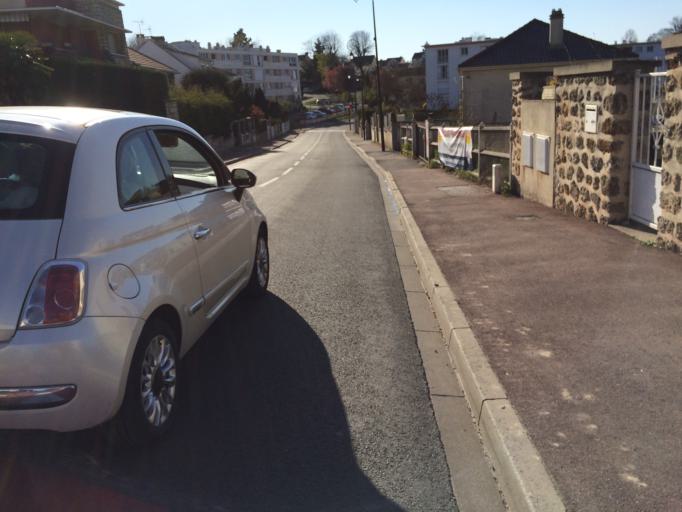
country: FR
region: Ile-de-France
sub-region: Departement de l'Essonne
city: Villebon-sur-Yvette
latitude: 48.6986
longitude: 2.2281
